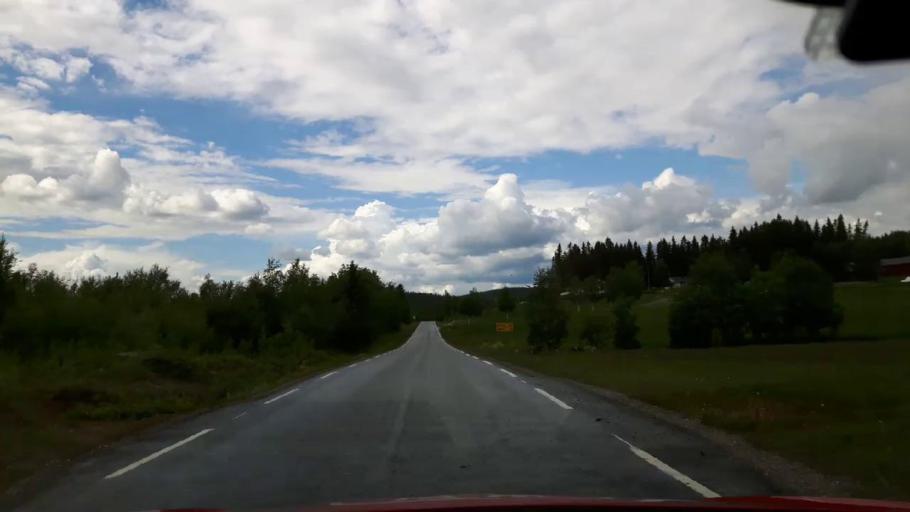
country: NO
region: Nord-Trondelag
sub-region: Lierne
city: Sandvika
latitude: 64.0951
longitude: 14.0409
